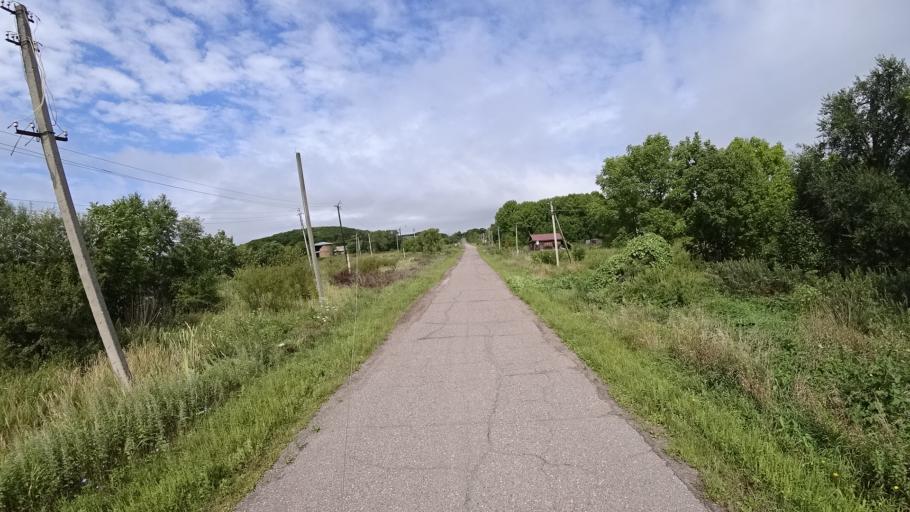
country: RU
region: Primorskiy
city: Lyalichi
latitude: 44.1365
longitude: 132.3875
